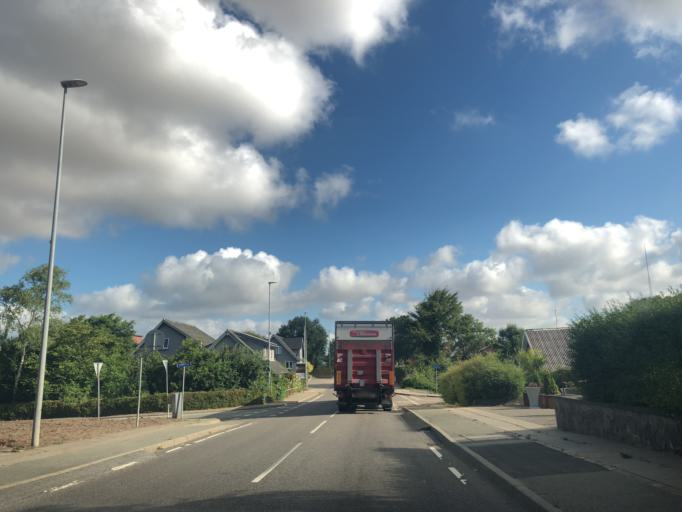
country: DK
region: Central Jutland
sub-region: Skive Kommune
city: Skive
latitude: 56.6510
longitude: 8.9329
